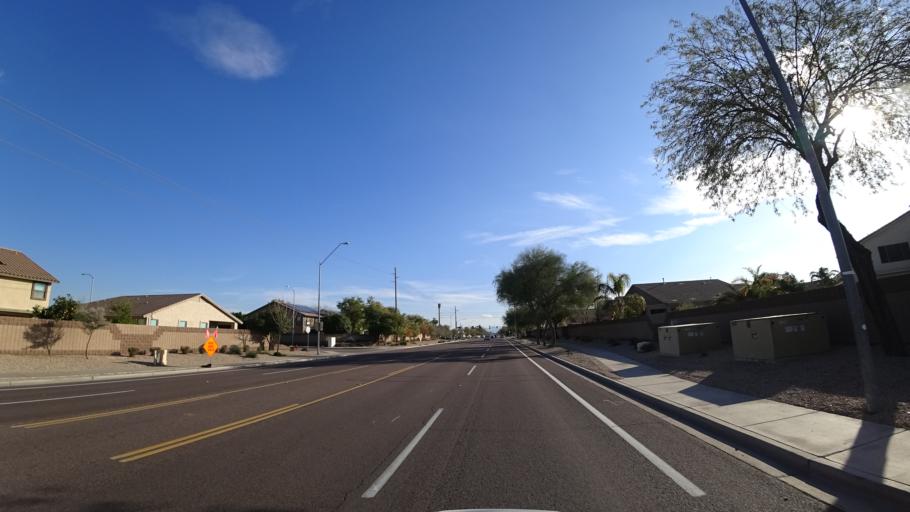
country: US
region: Arizona
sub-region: Maricopa County
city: Sun City
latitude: 33.6692
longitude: -112.2551
